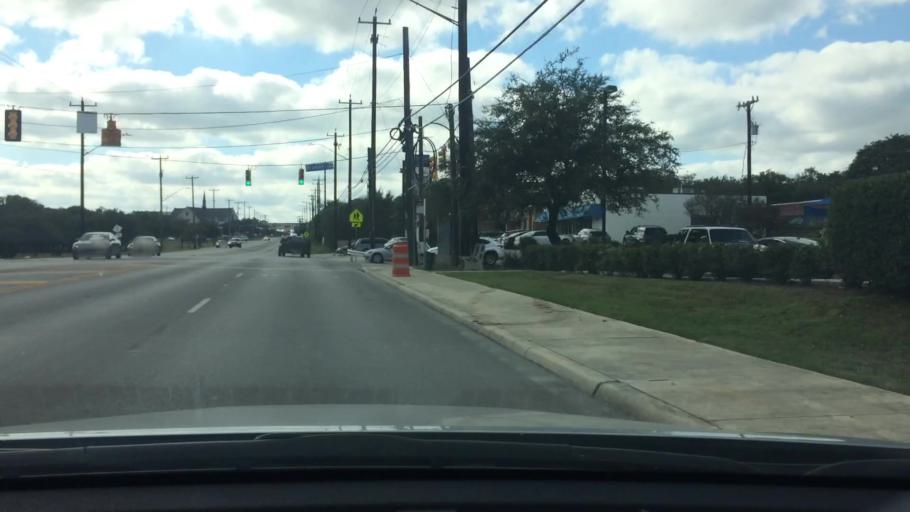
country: US
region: Texas
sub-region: Bexar County
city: Shavano Park
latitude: 29.5679
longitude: -98.5794
